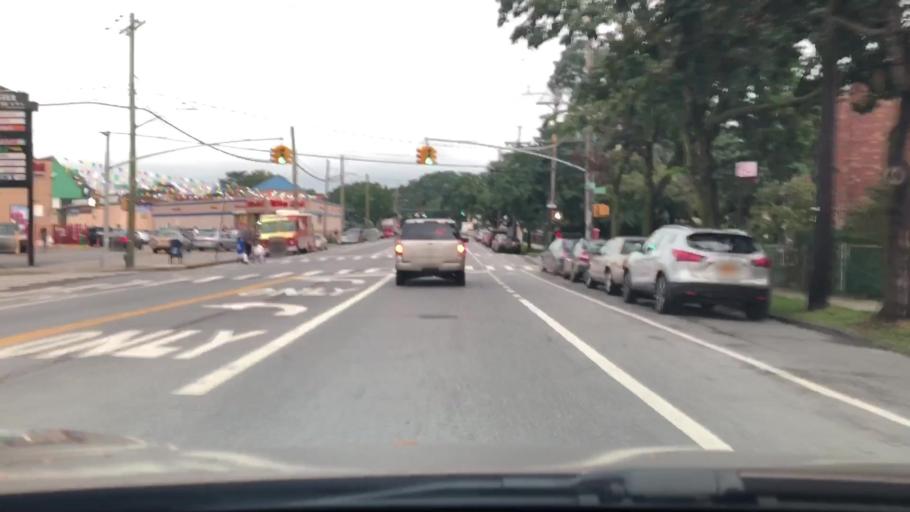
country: US
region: New York
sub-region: Bronx
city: Eastchester
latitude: 40.8893
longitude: -73.8446
